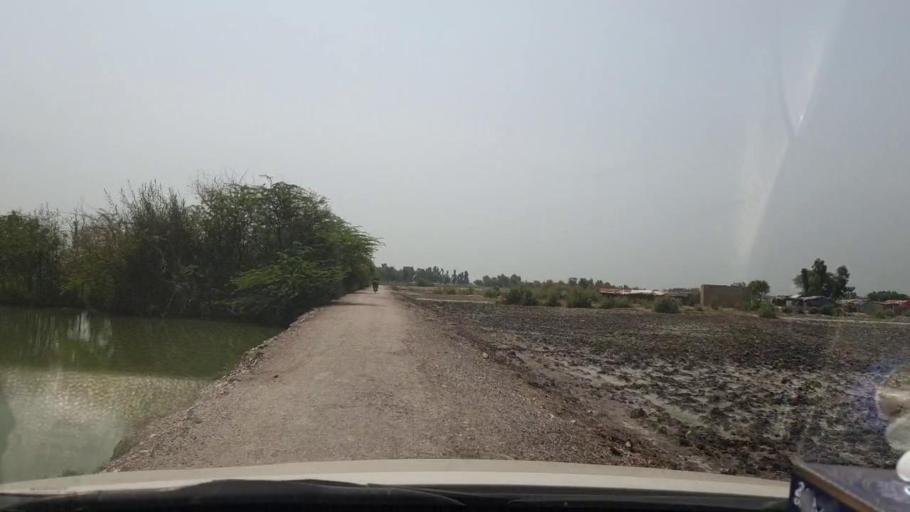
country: PK
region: Sindh
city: Shikarpur
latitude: 27.9886
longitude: 68.7052
